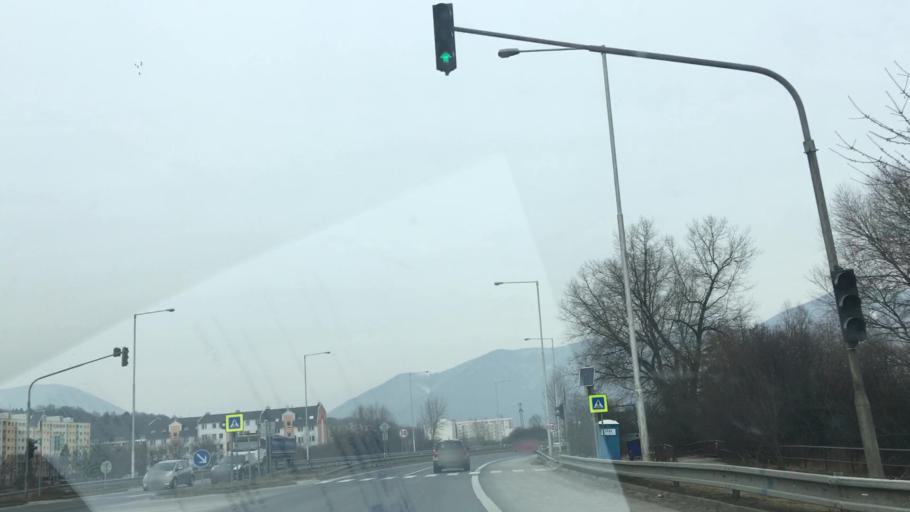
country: SK
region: Zilinsky
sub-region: Okres Martin
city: Martin
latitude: 49.0895
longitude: 18.9214
